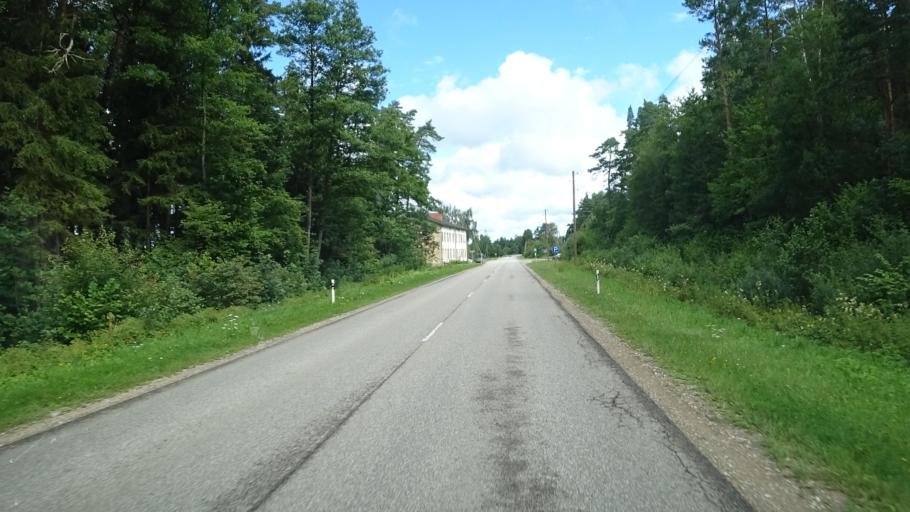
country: LV
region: Grobina
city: Grobina
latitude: 56.6759
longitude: 21.1382
